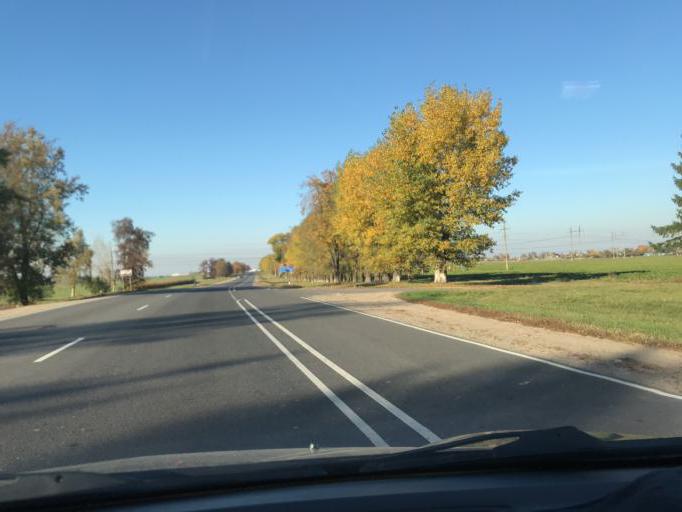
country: BY
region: Minsk
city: Slutsk
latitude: 53.0552
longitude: 27.5536
